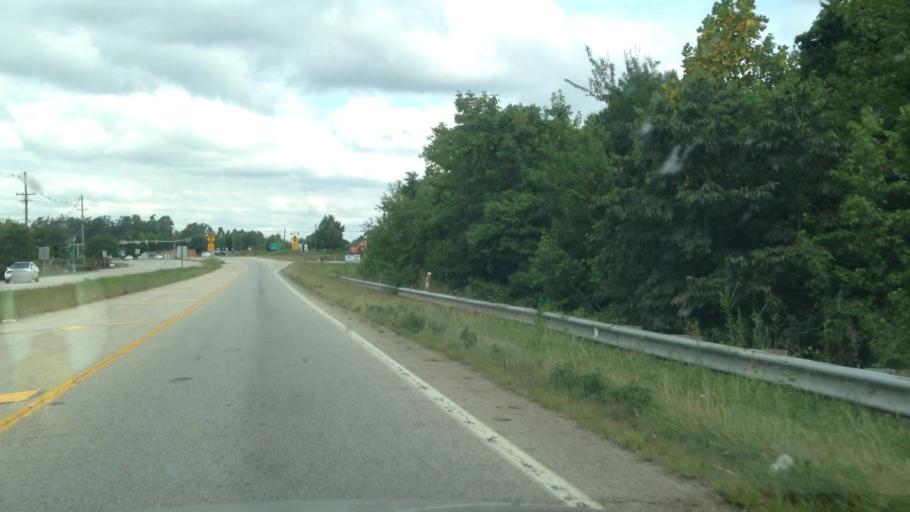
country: US
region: Virginia
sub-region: Pittsylvania County
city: Mount Hermon
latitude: 36.6940
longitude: -79.3668
